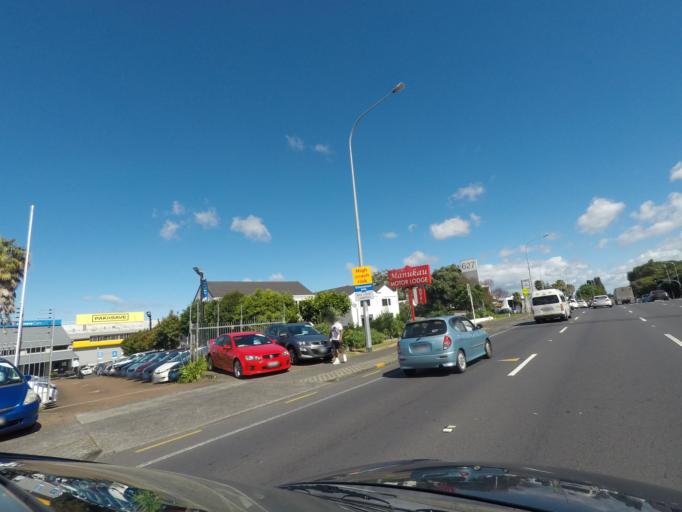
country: NZ
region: Auckland
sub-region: Auckland
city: Manukau City
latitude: -36.9878
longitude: 174.8822
